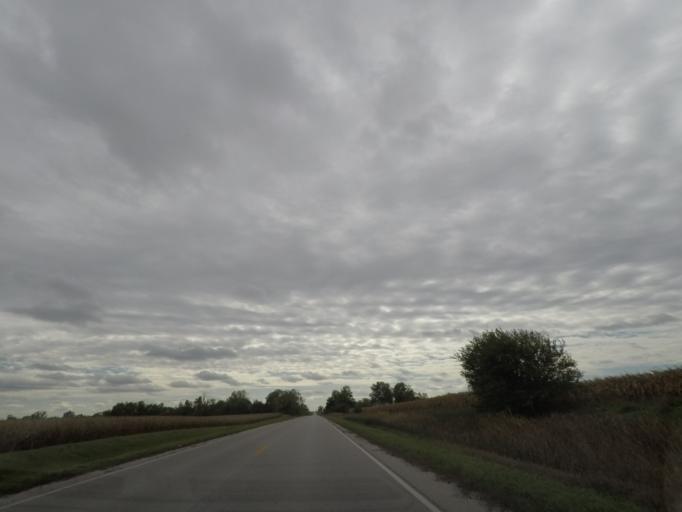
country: US
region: Iowa
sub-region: Story County
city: Huxley
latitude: 41.8727
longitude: -93.5315
